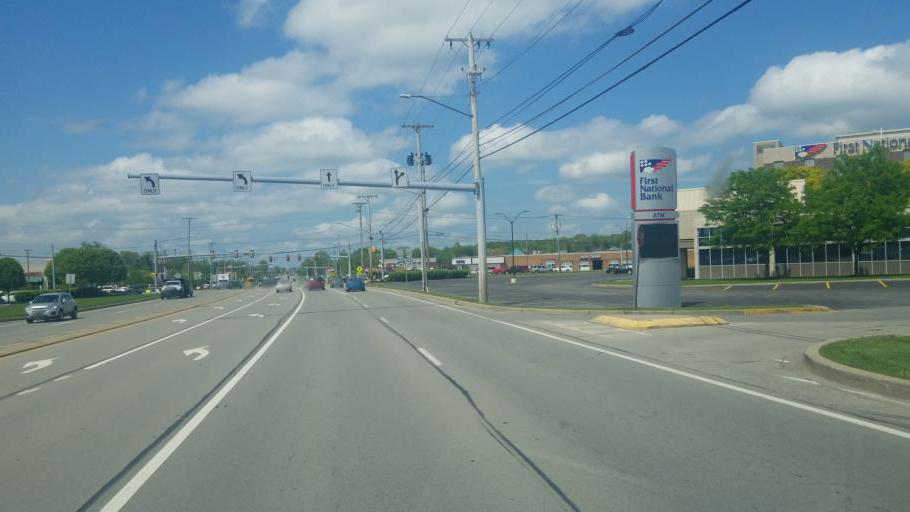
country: US
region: Pennsylvania
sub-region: Mercer County
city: Hermitage
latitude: 41.2320
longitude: -80.4496
